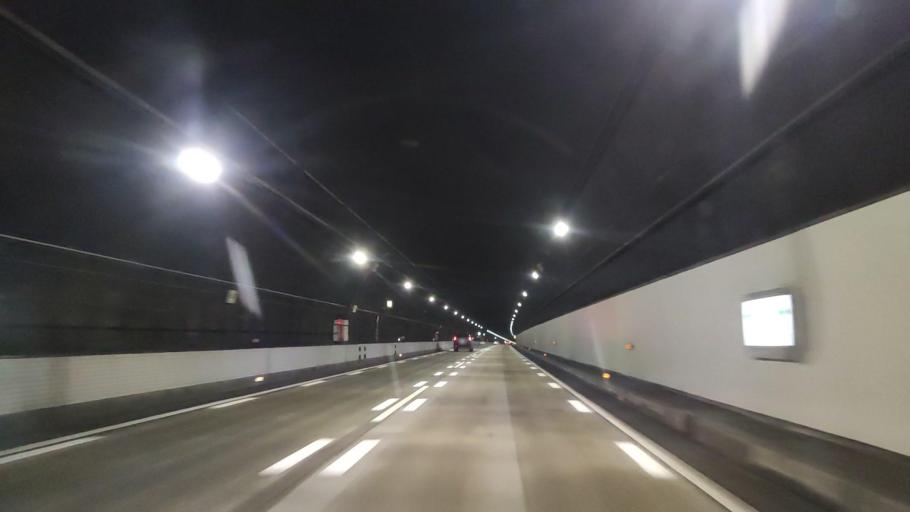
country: JP
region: Hiroshima
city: Fukuyama
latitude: 34.5041
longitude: 133.3276
